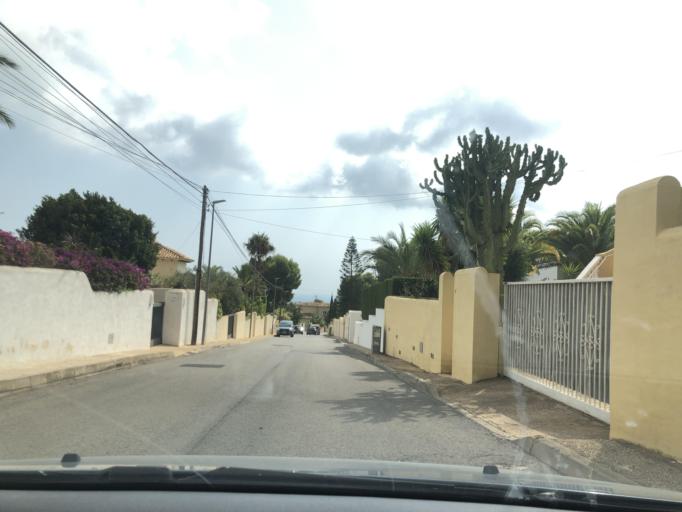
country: ES
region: Valencia
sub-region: Provincia de Alicante
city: Altea
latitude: 38.6385
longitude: -0.0670
